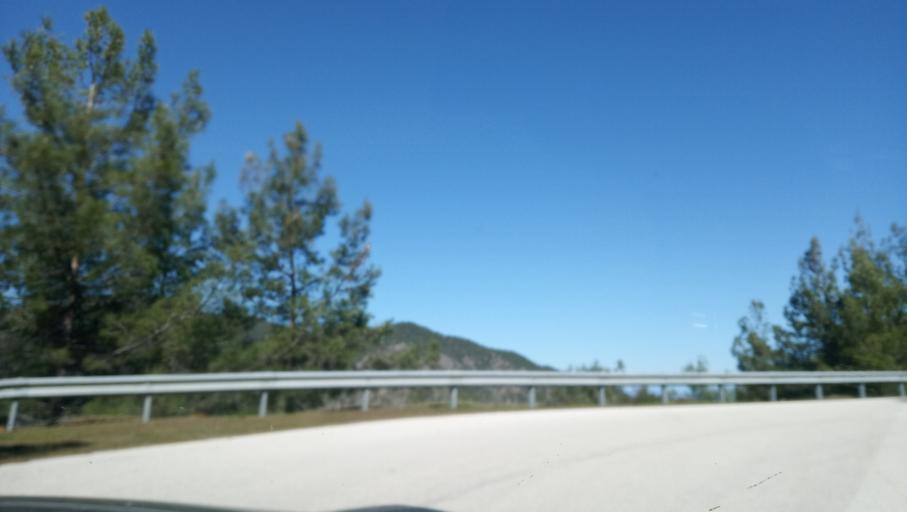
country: CY
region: Lefkosia
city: Lefka
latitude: 35.0682
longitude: 32.7502
